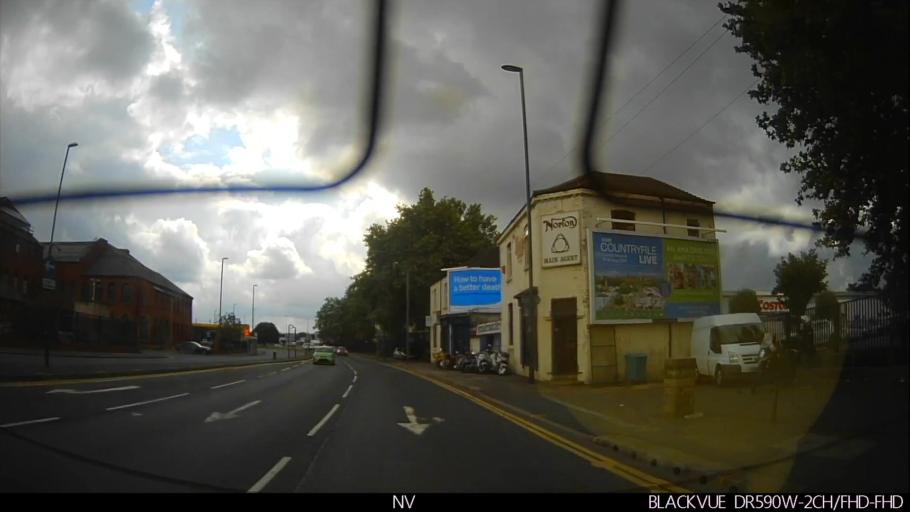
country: GB
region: England
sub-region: City and Borough of Leeds
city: Leeds
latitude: 53.7878
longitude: -1.5353
